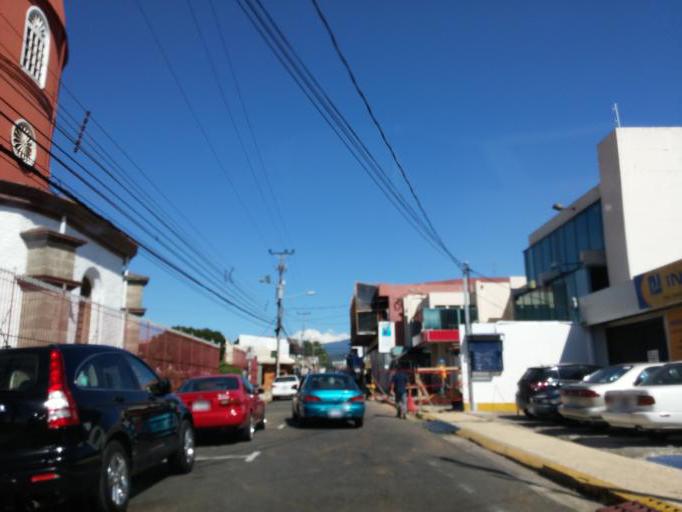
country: CR
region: Alajuela
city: Alajuela
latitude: 10.0167
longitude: -84.2126
